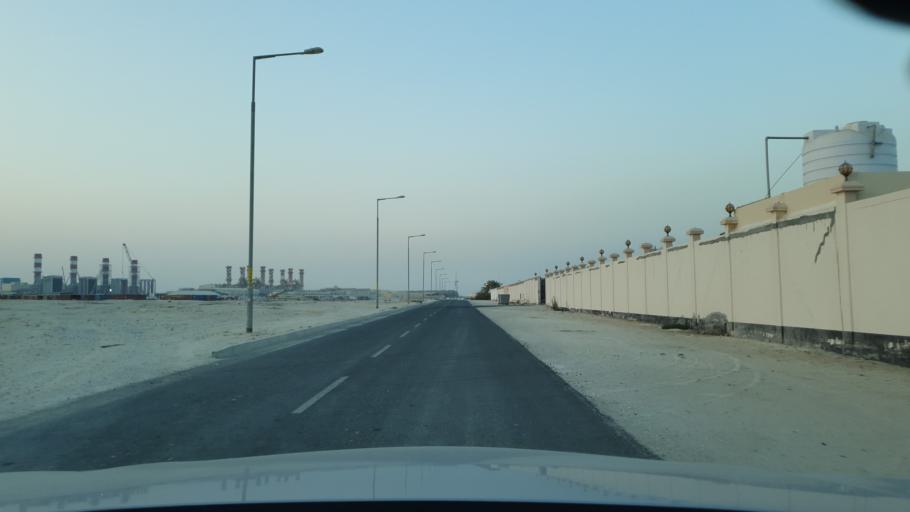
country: BH
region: Central Governorate
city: Dar Kulayb
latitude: 25.9593
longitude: 50.6113
